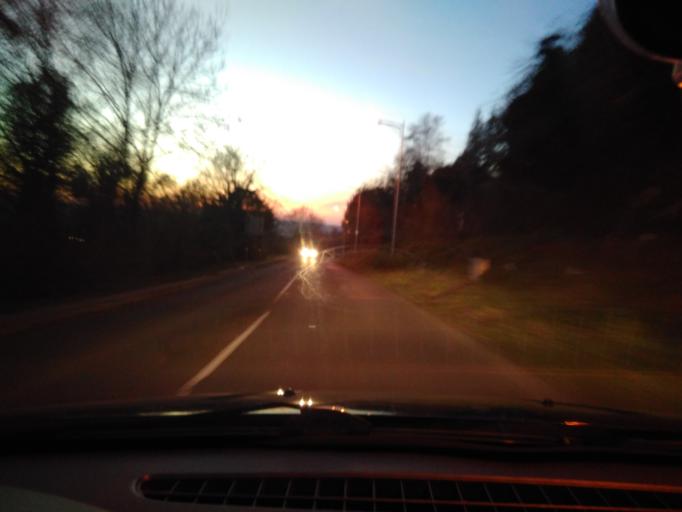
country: FR
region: Picardie
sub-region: Departement de l'Aisne
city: Laon
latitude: 49.5617
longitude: 3.6088
